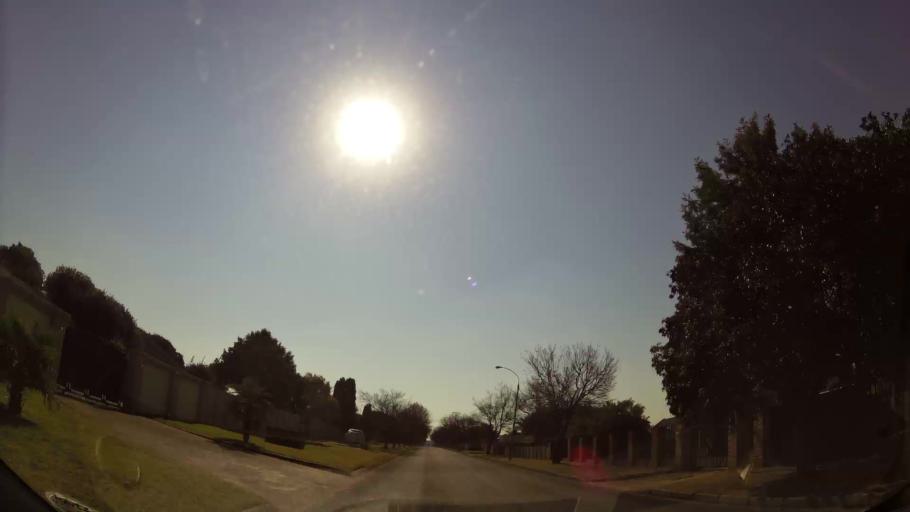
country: ZA
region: Gauteng
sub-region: Ekurhuleni Metropolitan Municipality
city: Boksburg
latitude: -26.1594
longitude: 28.2580
